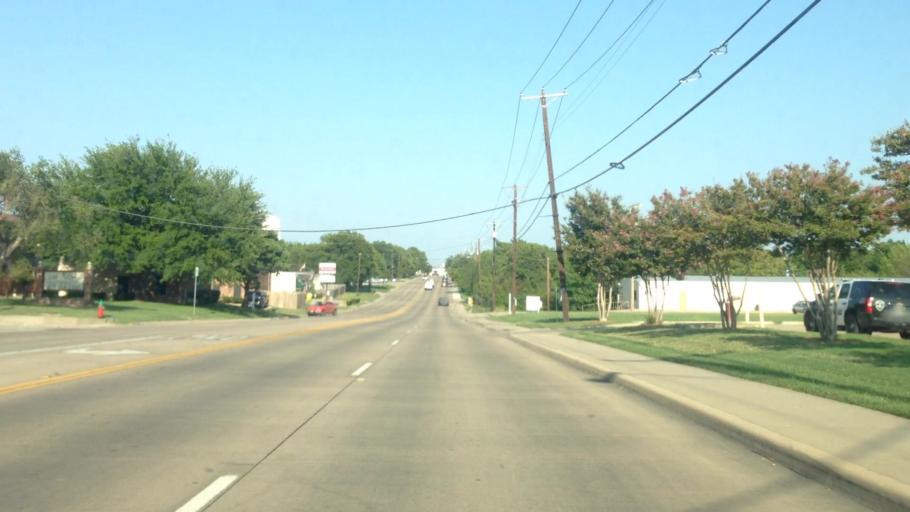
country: US
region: Texas
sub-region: Tarrant County
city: Haltom City
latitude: 32.8096
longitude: -97.2724
